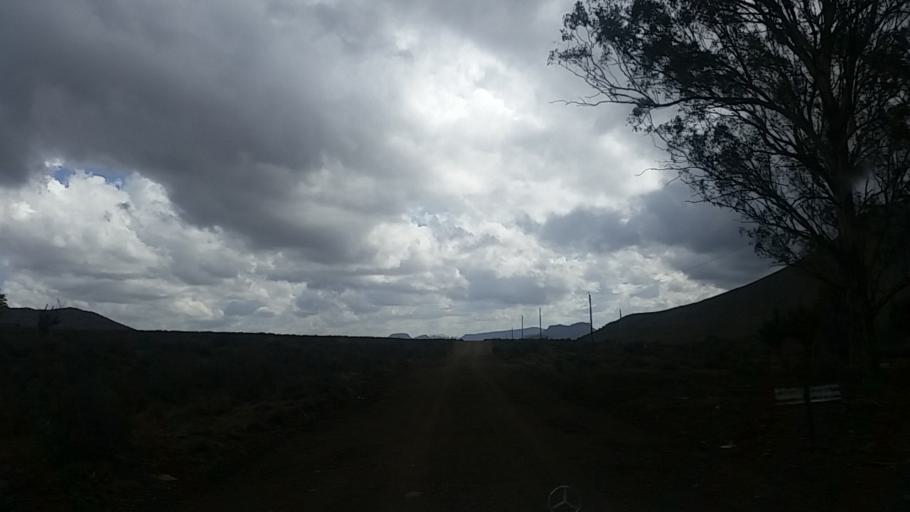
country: ZA
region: Eastern Cape
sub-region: Chris Hani District Municipality
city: Middelburg
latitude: -31.7897
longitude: 24.6713
